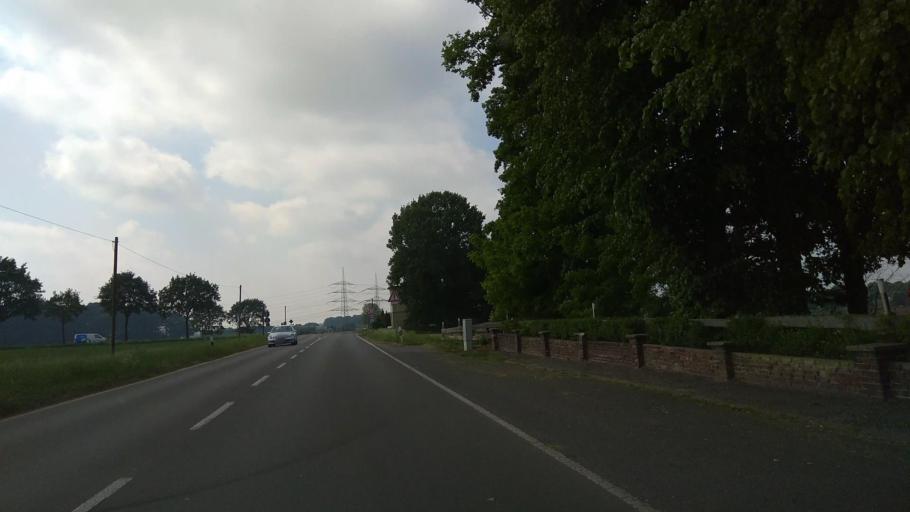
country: DE
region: North Rhine-Westphalia
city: Marl
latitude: 51.6249
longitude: 7.0859
